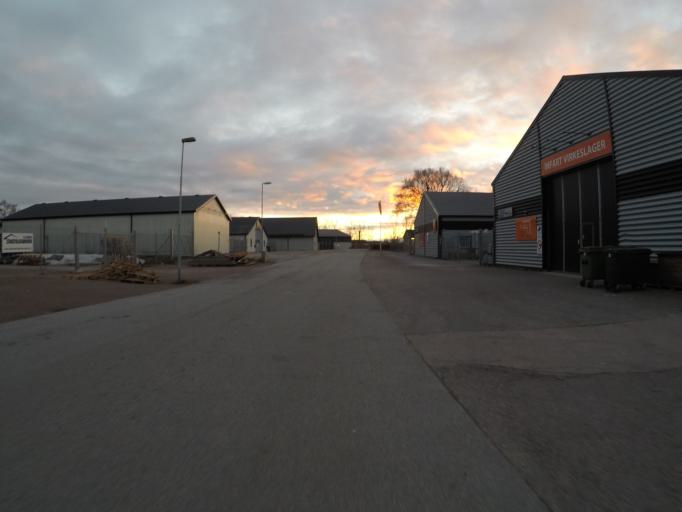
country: SE
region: Skane
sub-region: Sjobo Kommun
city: Sjoebo
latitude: 55.6443
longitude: 13.6924
